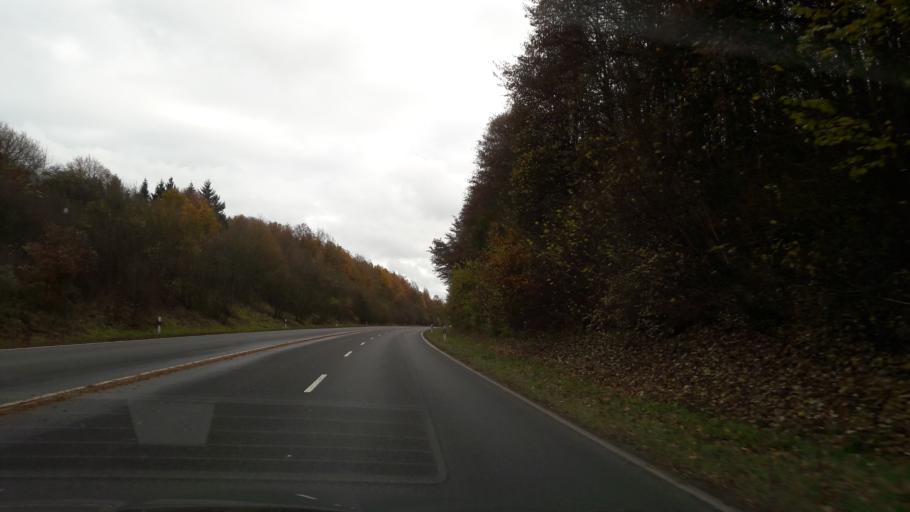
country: DE
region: Rheinland-Pfalz
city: Kenn
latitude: 49.7929
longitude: 6.7343
